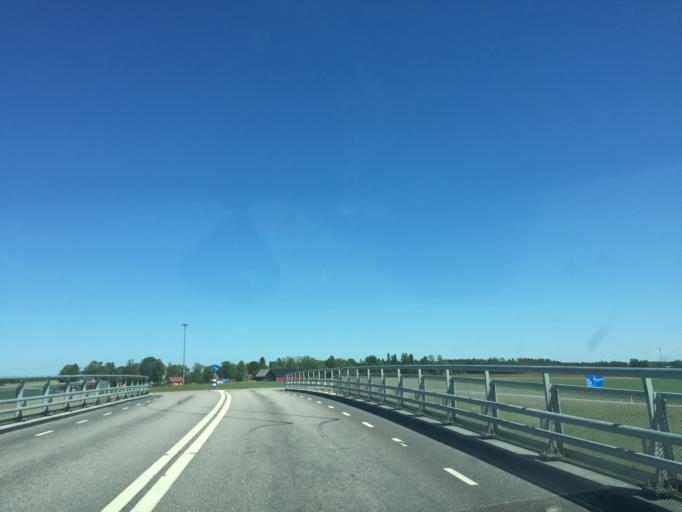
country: SE
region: OEstergoetland
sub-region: Mjolby Kommun
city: Mjolby
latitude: 58.4029
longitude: 15.0913
